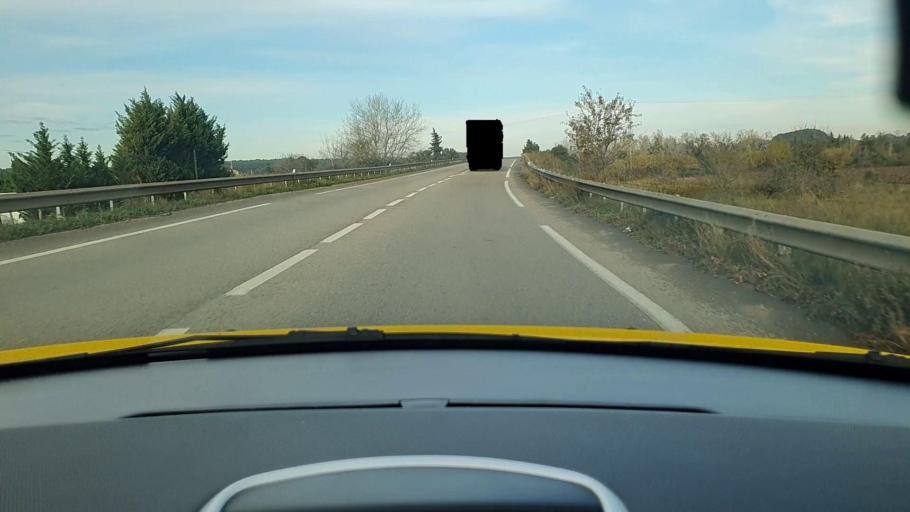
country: FR
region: Languedoc-Roussillon
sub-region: Departement du Gard
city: Beaucaire
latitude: 43.7948
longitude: 4.6111
